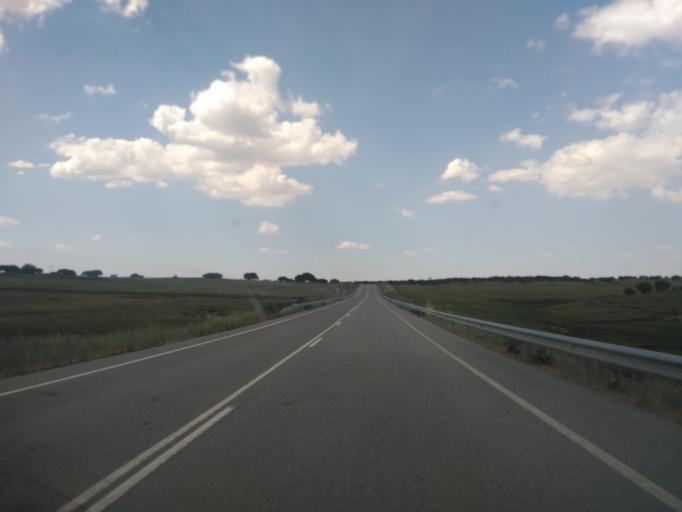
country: ES
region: Castille and Leon
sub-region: Provincia de Salamanca
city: Buenavista
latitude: 40.7849
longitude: -5.6302
